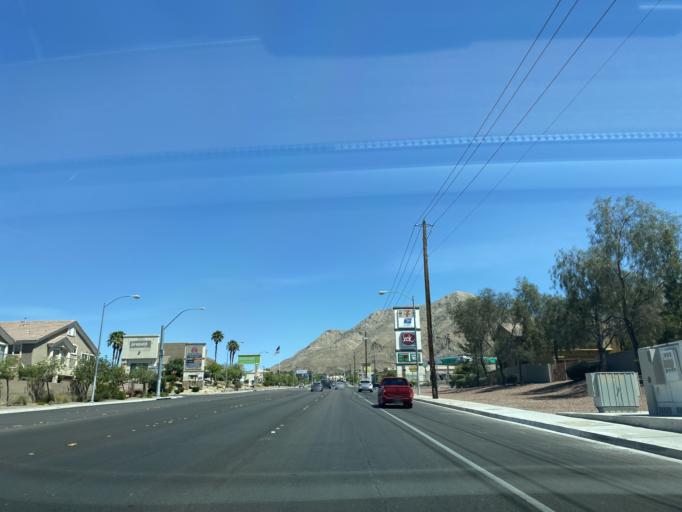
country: US
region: Nevada
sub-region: Clark County
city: Sunrise Manor
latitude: 36.1958
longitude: -115.0320
